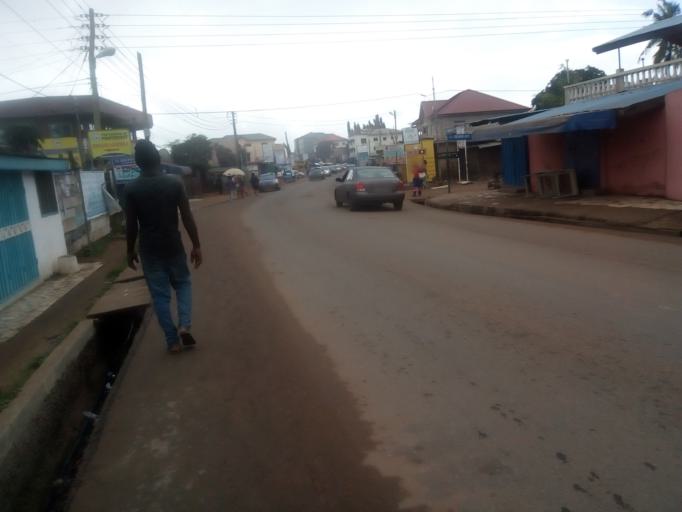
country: GH
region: Greater Accra
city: Dome
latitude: 5.6070
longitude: -0.2557
